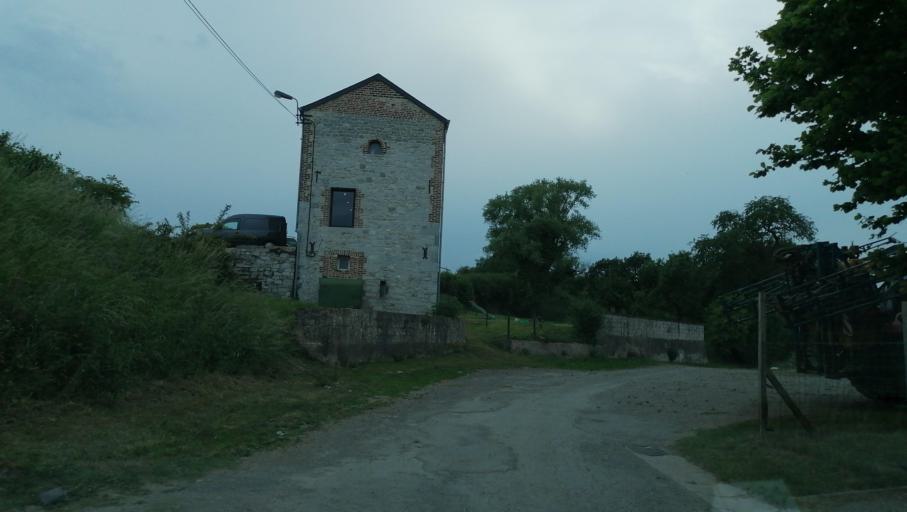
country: BE
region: Wallonia
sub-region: Province du Hainaut
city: Beaumont
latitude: 50.2006
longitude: 4.1679
